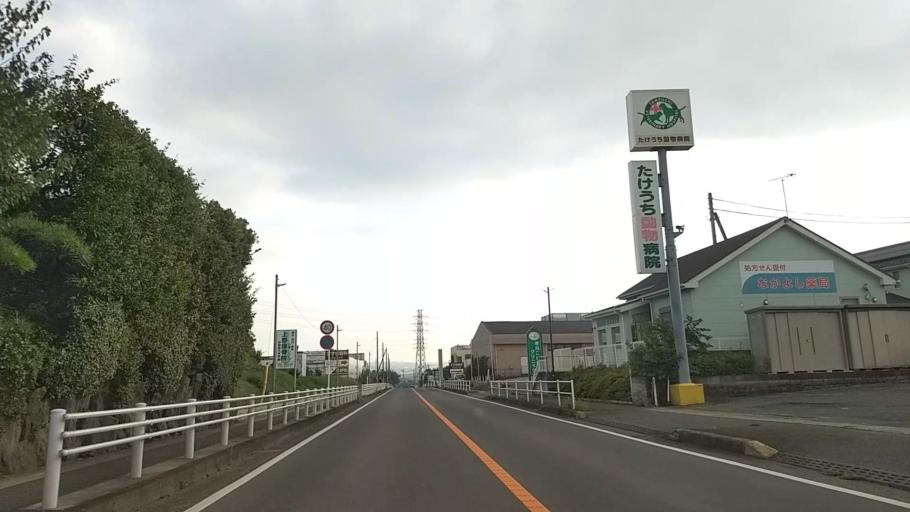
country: JP
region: Kanagawa
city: Isehara
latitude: 35.3904
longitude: 139.3040
